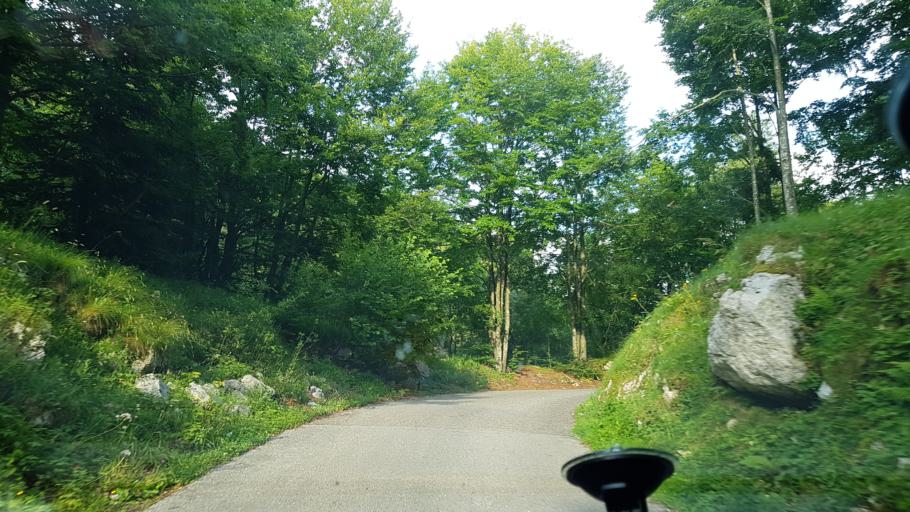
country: IT
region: Friuli Venezia Giulia
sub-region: Provincia di Udine
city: Prato
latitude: 46.3368
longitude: 13.3193
